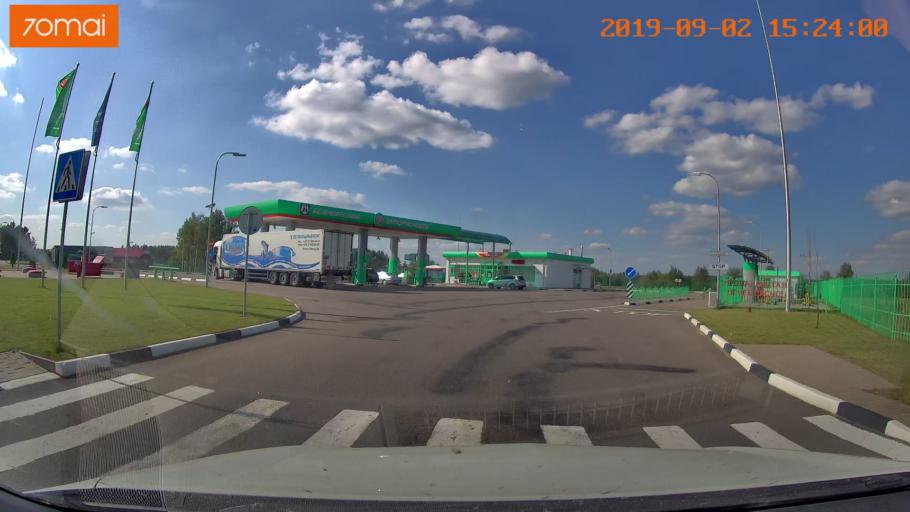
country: BY
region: Mogilev
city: Byalynichy
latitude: 53.9100
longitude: 29.4121
